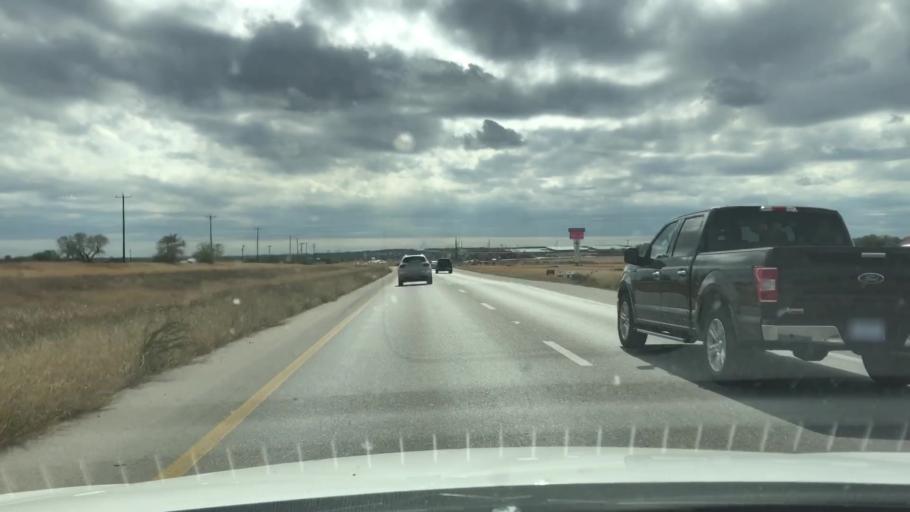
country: US
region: Texas
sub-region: Bexar County
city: Converse
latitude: 29.5093
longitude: -98.2869
